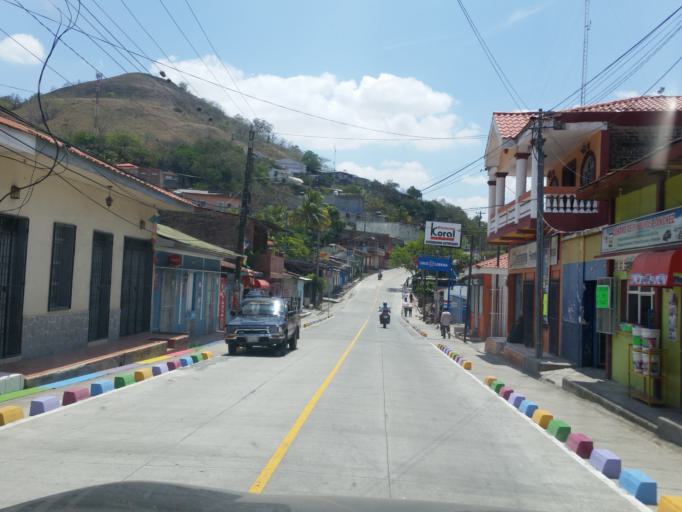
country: NI
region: Boaco
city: Boaco
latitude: 12.4697
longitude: -85.6582
